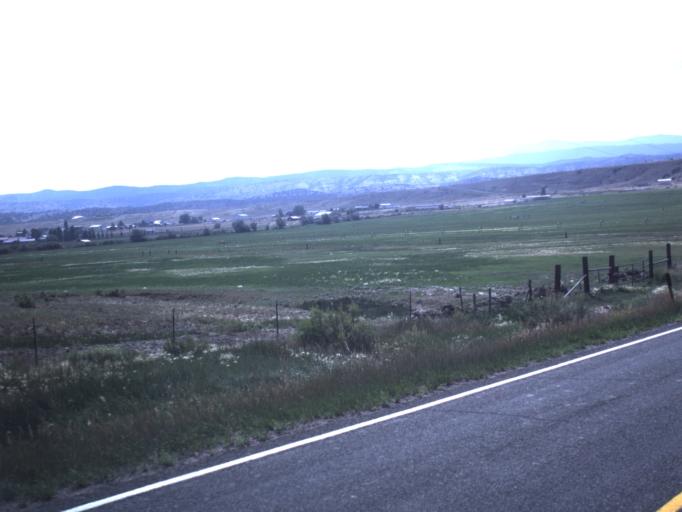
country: US
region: Utah
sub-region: Daggett County
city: Manila
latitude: 40.9798
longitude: -109.7227
